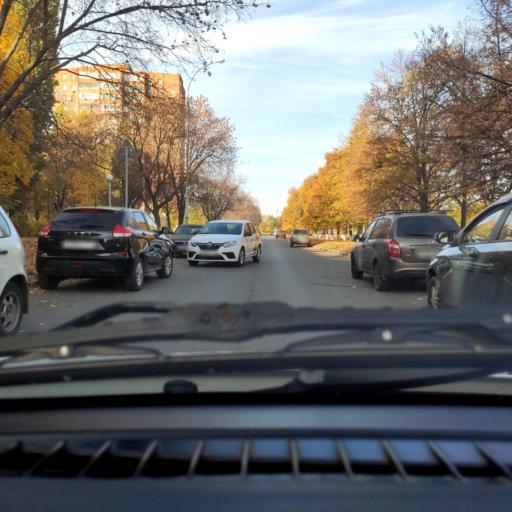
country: RU
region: Samara
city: Tol'yatti
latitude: 53.5207
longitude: 49.2643
